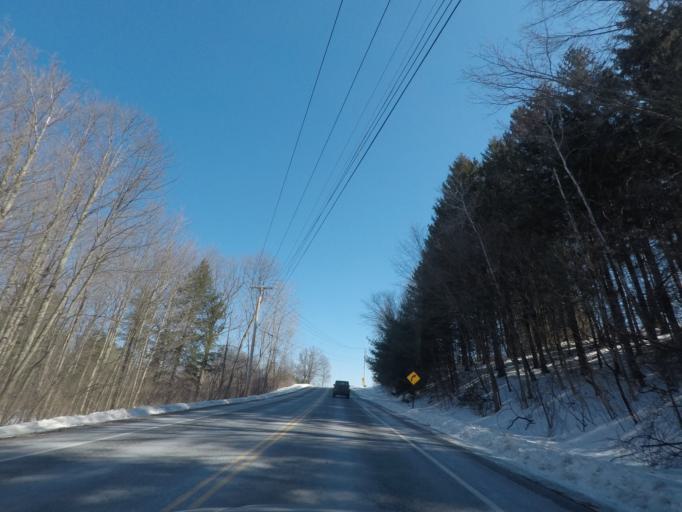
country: US
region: New York
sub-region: Saratoga County
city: Saratoga Springs
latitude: 43.0543
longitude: -73.7589
